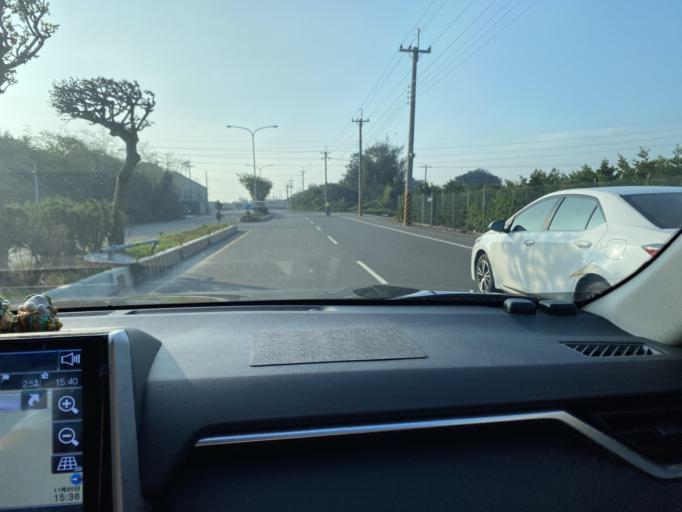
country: TW
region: Taiwan
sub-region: Changhua
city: Chang-hua
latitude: 23.9599
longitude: 120.3633
